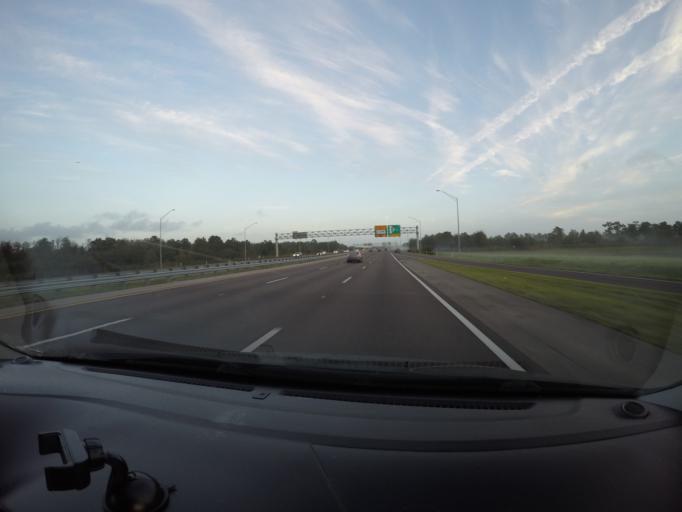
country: US
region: Florida
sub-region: Orange County
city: Azalea Park
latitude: 28.4813
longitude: -81.2403
